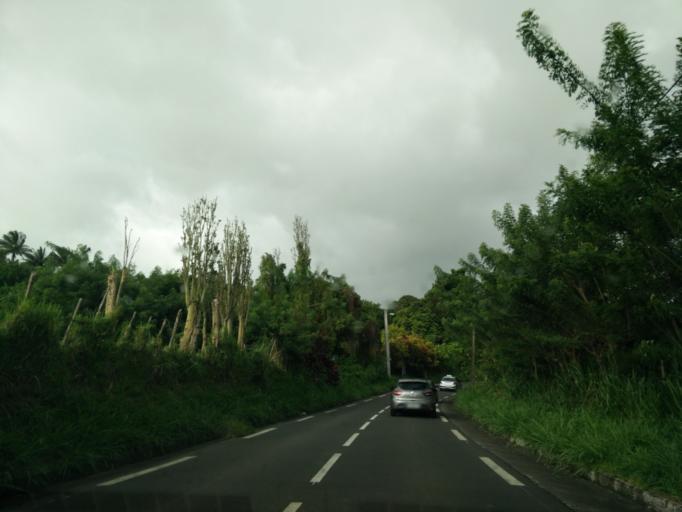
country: MQ
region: Martinique
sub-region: Martinique
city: Le Morne-Rouge
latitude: 14.7670
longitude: -61.1475
